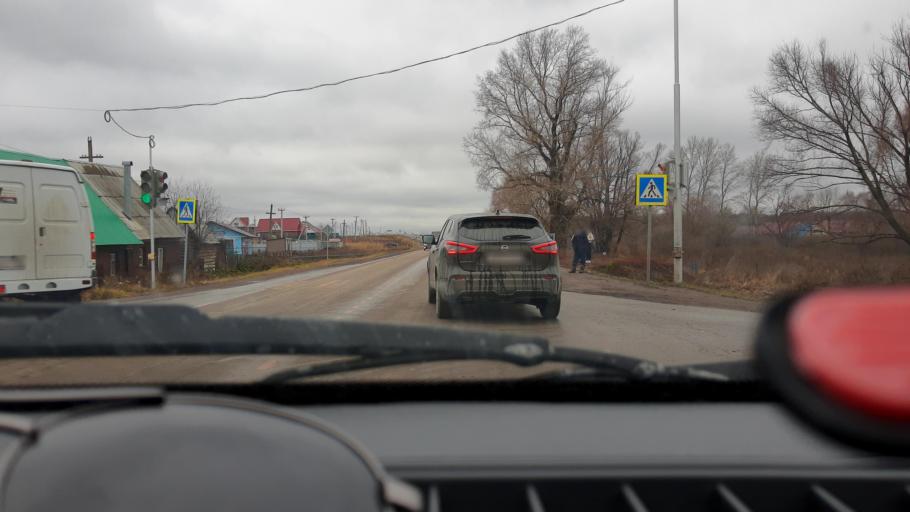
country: RU
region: Bashkortostan
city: Avdon
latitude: 54.7353
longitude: 55.8030
